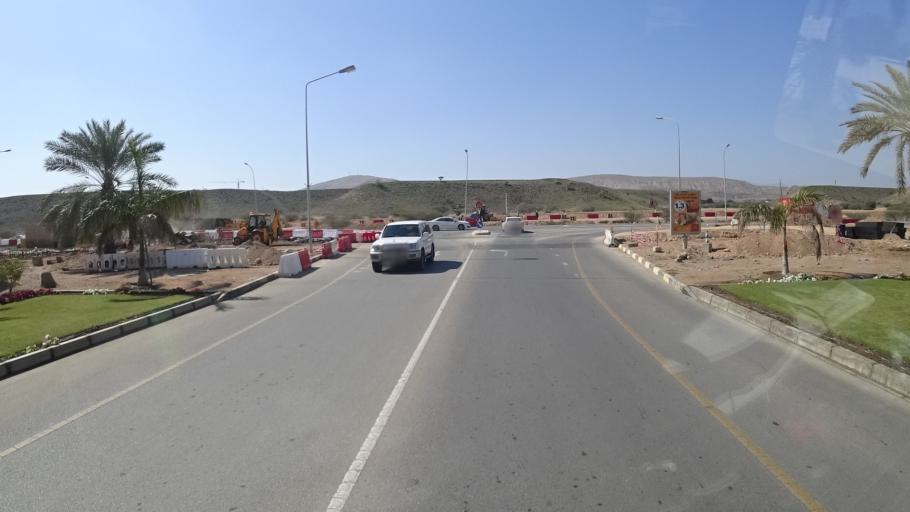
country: OM
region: Muhafazat Masqat
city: As Sib al Jadidah
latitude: 23.5811
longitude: 58.1754
